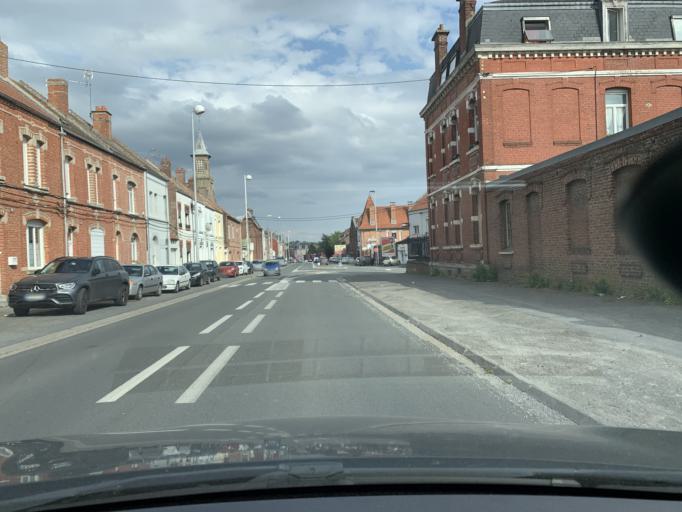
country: FR
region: Nord-Pas-de-Calais
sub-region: Departement du Nord
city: Neuville-Saint-Remy
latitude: 50.1785
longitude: 3.2132
